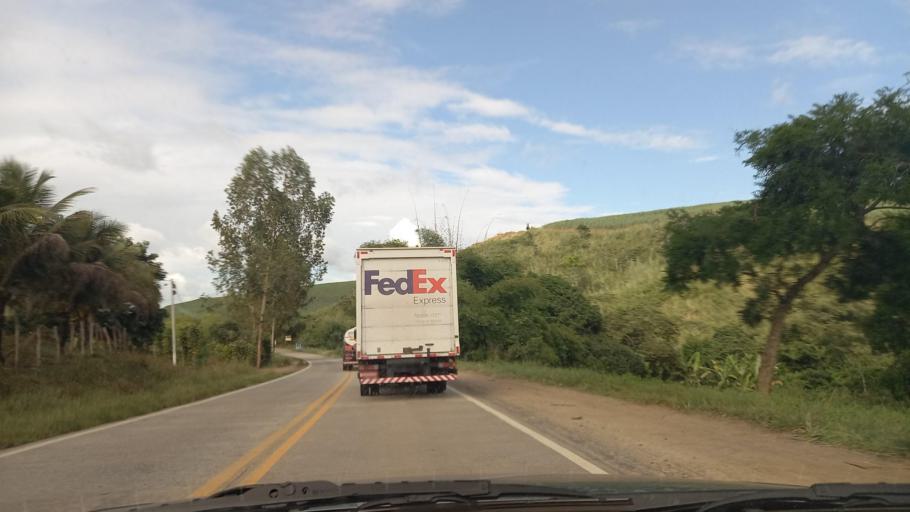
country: BR
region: Pernambuco
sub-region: Catende
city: Catende
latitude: -8.6962
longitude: -35.6612
